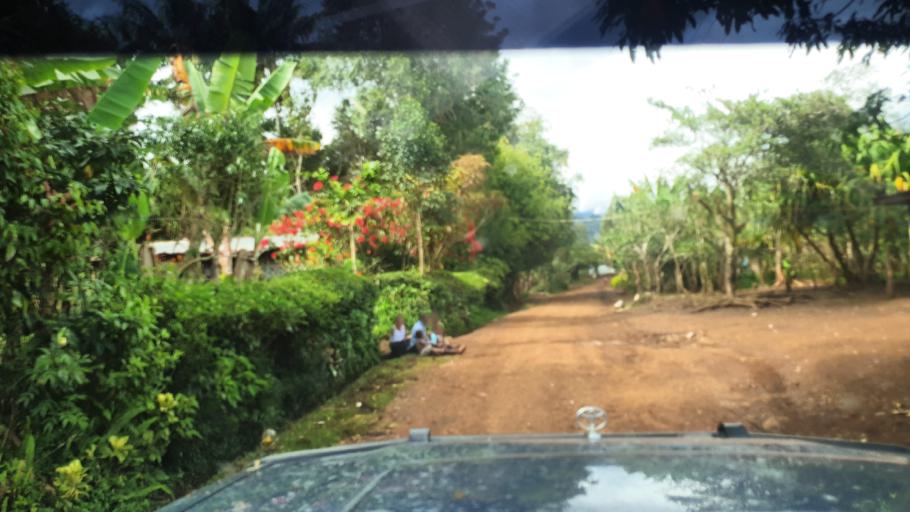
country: PG
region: Jiwaka
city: Minj
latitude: -5.8976
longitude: 144.8127
